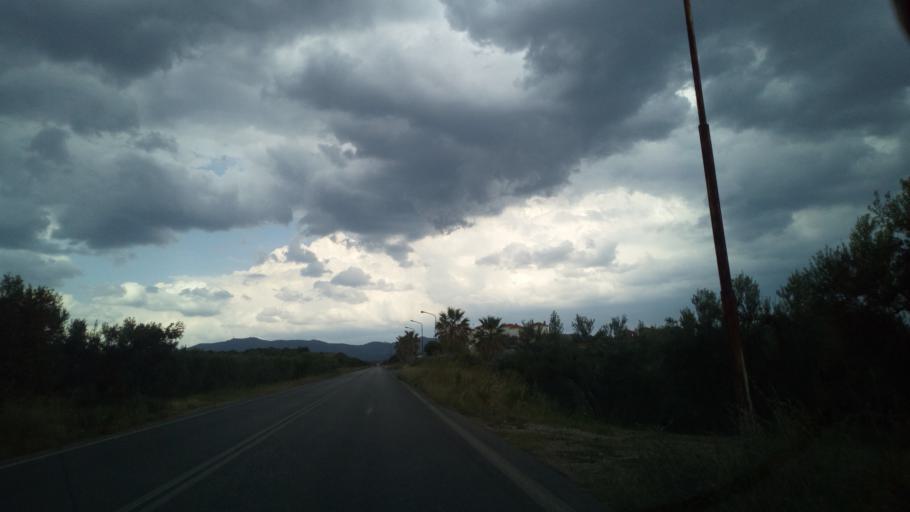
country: GR
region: Central Macedonia
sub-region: Nomos Chalkidikis
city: Kalyves Polygyrou
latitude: 40.3006
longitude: 23.4332
